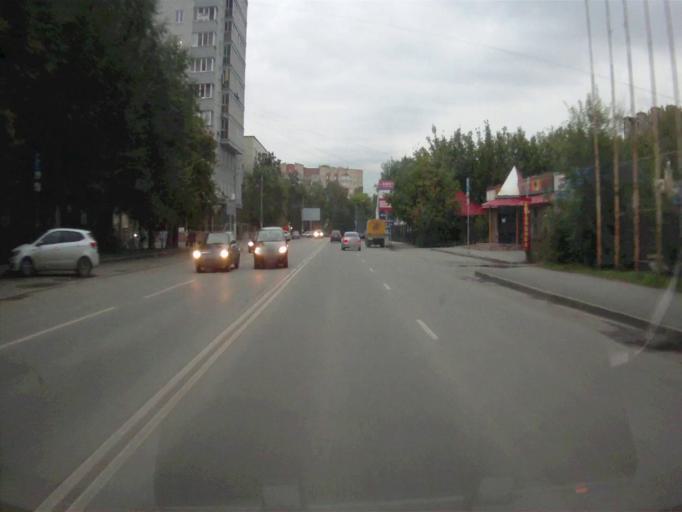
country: RU
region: Chelyabinsk
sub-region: Gorod Chelyabinsk
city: Chelyabinsk
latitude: 55.1521
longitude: 61.3984
